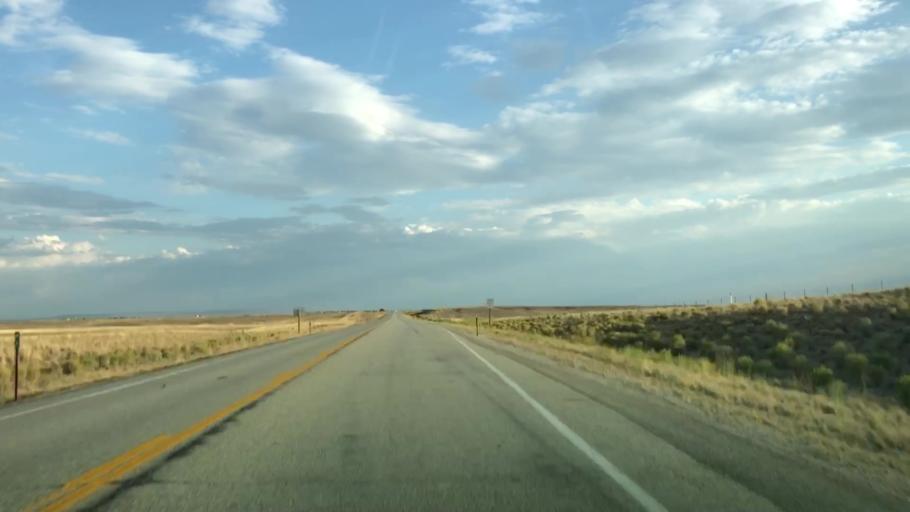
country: US
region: Wyoming
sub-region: Sweetwater County
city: North Rock Springs
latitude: 42.1852
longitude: -109.4789
